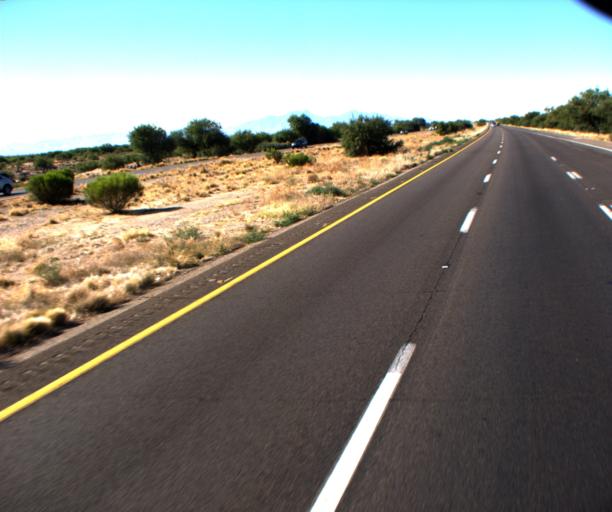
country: US
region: Arizona
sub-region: Pima County
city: Drexel Heights
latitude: 32.1010
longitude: -110.9935
